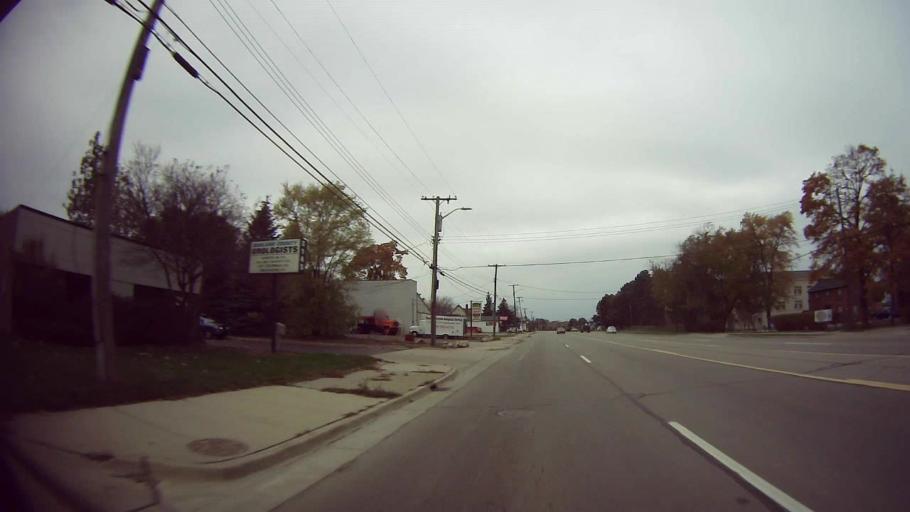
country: US
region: Michigan
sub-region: Oakland County
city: Waterford
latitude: 42.6754
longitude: -83.3508
